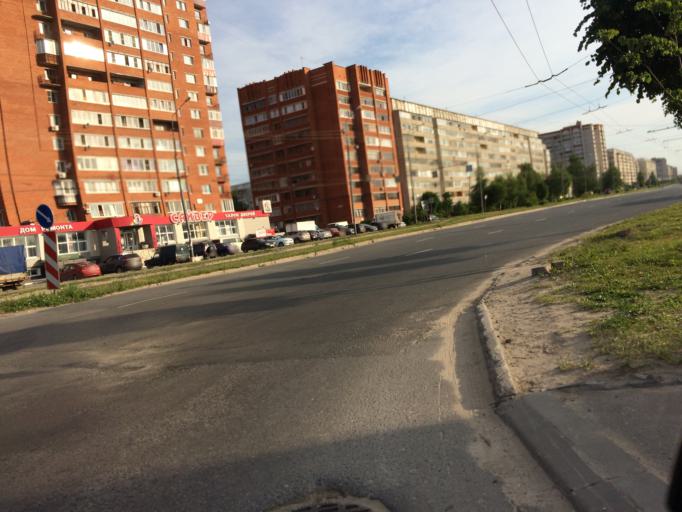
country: RU
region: Mariy-El
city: Yoshkar-Ola
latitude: 56.6254
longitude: 47.9257
